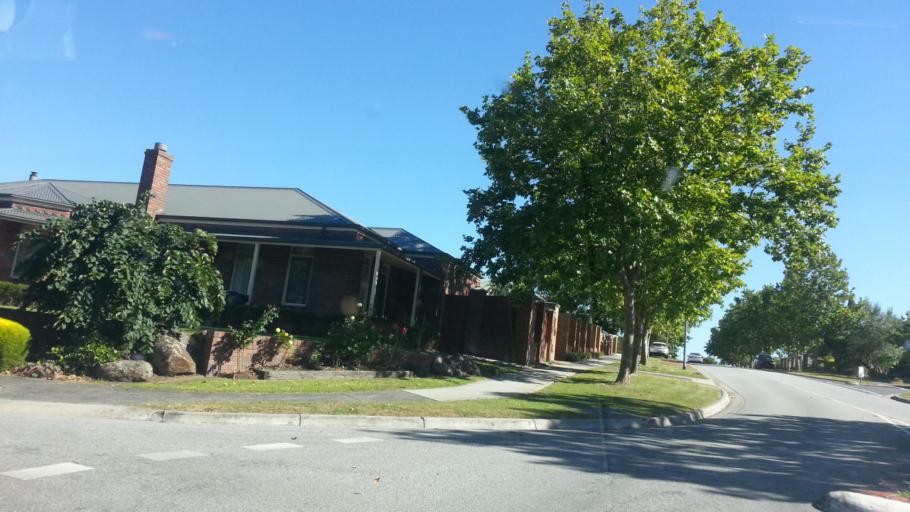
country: AU
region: Victoria
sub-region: Knox
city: Rowville
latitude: -37.9244
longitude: 145.2537
